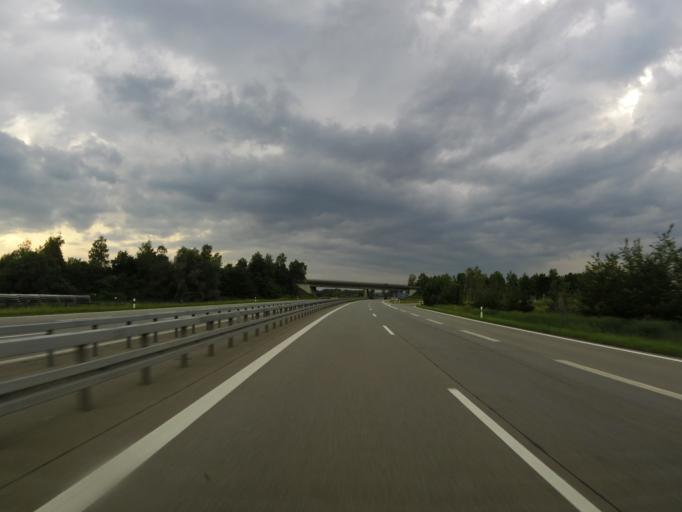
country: DE
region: Bavaria
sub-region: Lower Bavaria
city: Wallersdorf
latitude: 48.7289
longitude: 12.7294
